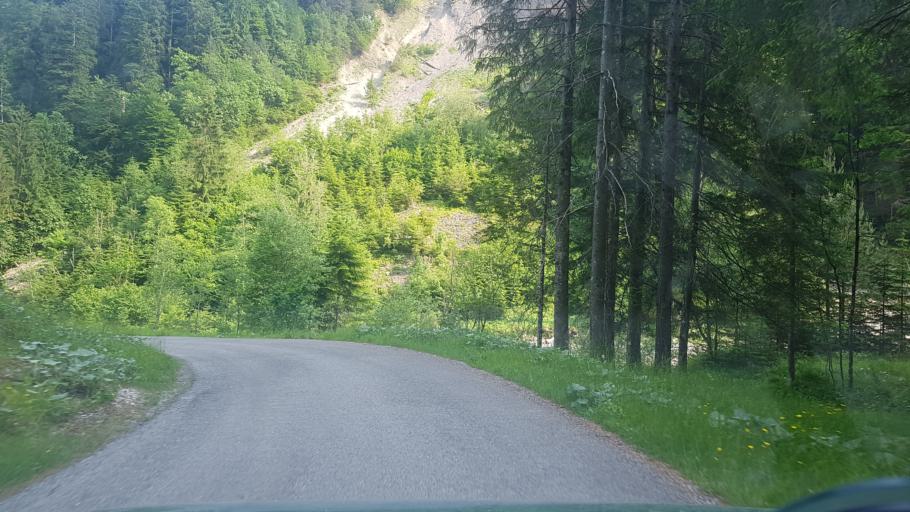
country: IT
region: Friuli Venezia Giulia
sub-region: Provincia di Udine
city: Pontebba
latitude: 46.5256
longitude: 13.2363
